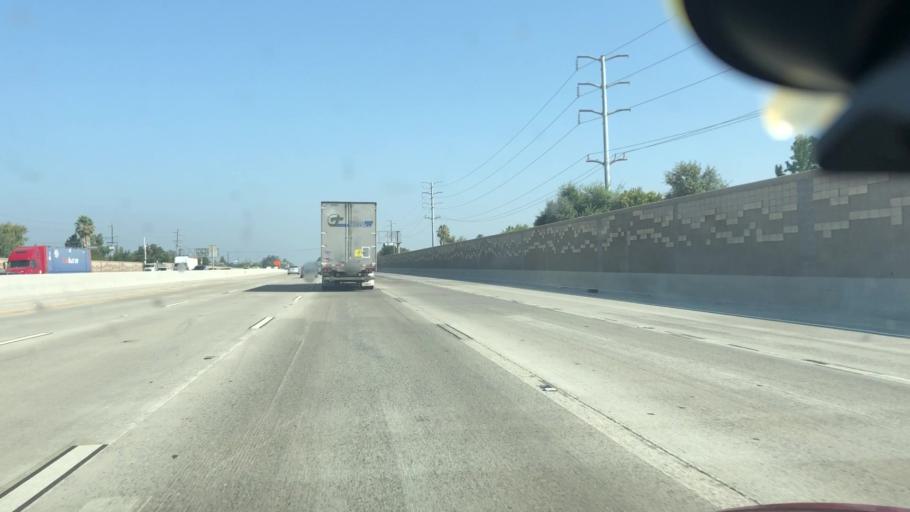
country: US
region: California
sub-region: San Joaquin County
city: Lincoln Village
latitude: 38.0119
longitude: -121.3540
